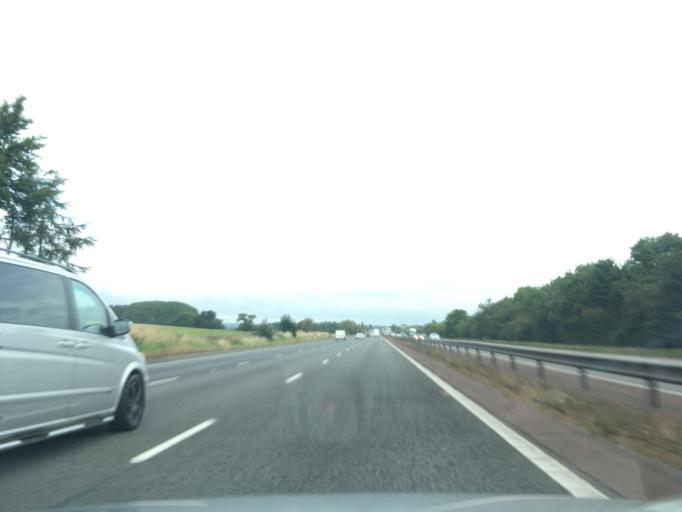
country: GB
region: England
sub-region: Oxfordshire
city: Adderbury
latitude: 52.0398
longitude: -1.3042
